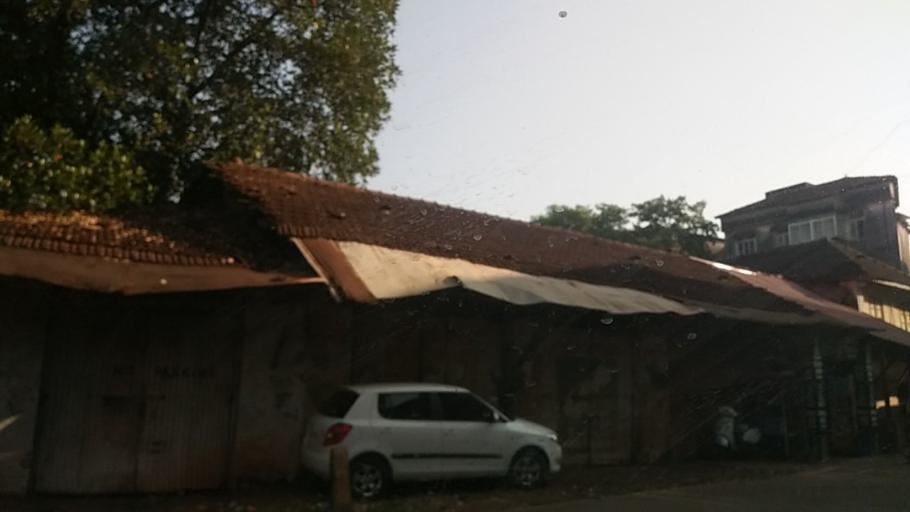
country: IN
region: Goa
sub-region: South Goa
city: Madgaon
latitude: 15.2767
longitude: 73.9541
